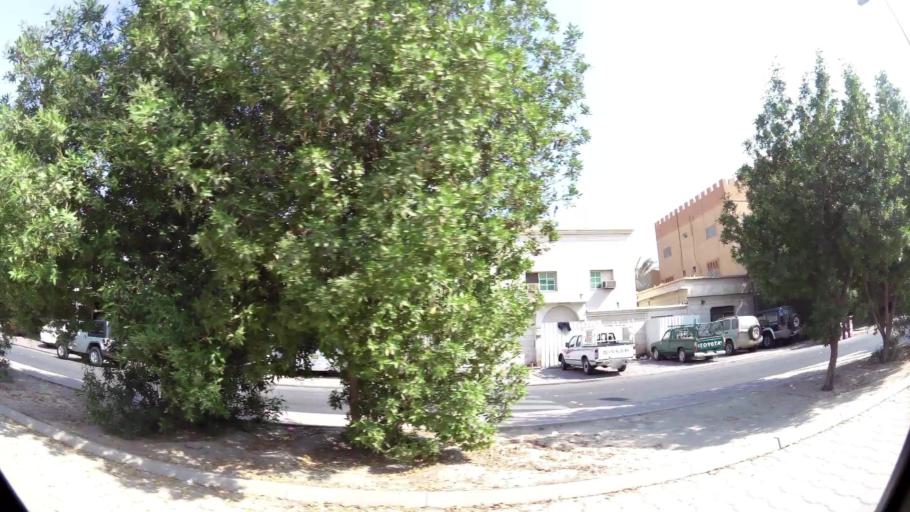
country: KW
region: Al Ahmadi
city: Al Fahahil
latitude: 29.0761
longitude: 48.1176
